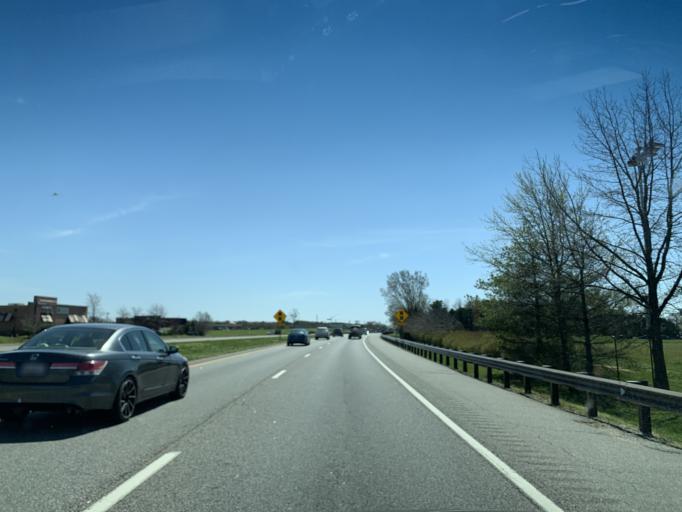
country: US
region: Maryland
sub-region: Talbot County
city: Easton
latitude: 38.7956
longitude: -76.0605
